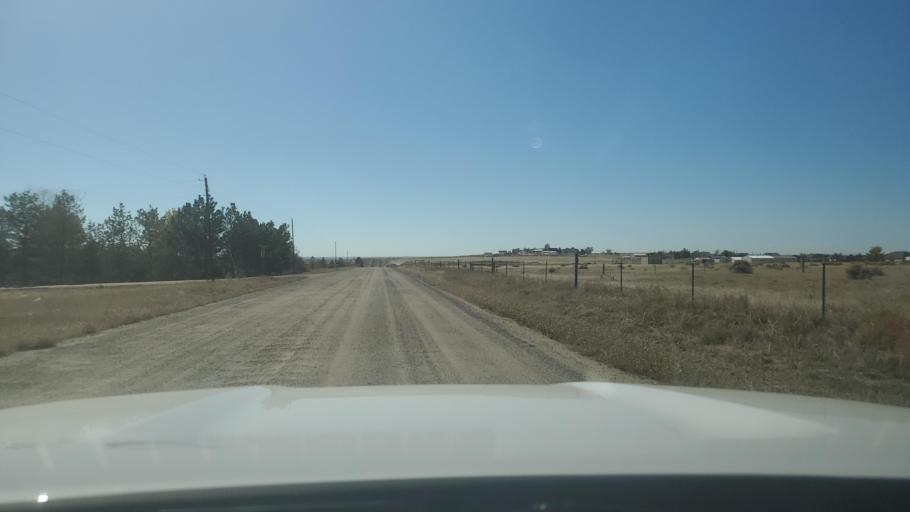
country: US
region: Colorado
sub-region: Adams County
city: Bennett
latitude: 39.7723
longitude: -104.3770
